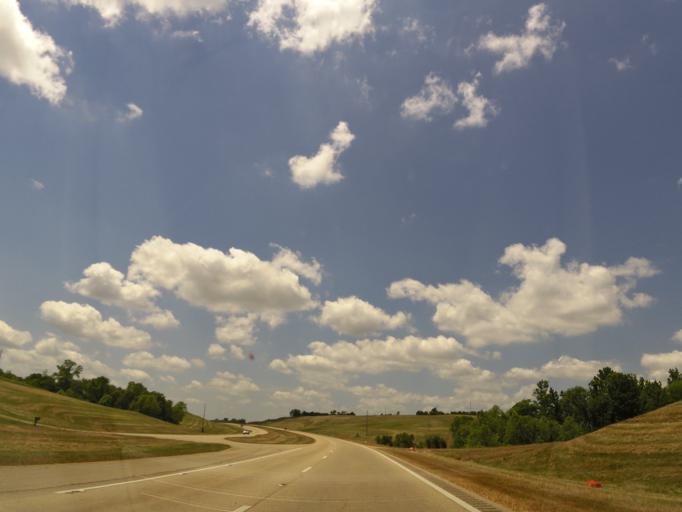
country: US
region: Mississippi
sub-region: Pontotoc County
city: Pontotoc
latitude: 34.2897
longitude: -88.9575
